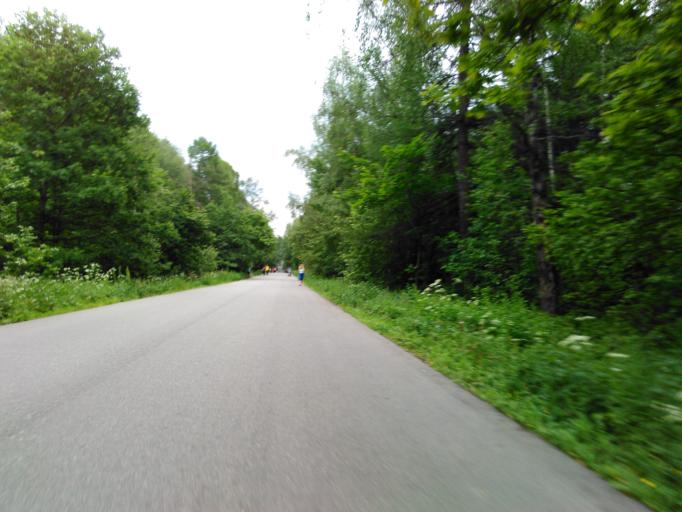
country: RU
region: Moscow
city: Yasenevo
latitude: 55.6245
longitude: 37.5196
